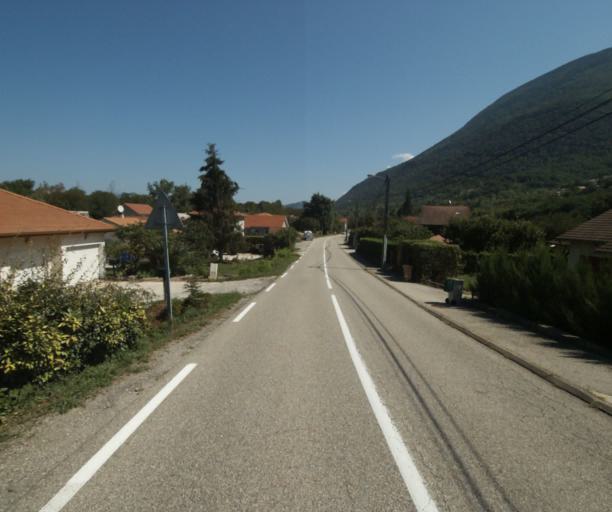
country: FR
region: Rhone-Alpes
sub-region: Departement de l'Isere
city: Saint-Georges-de-Commiers
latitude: 45.0446
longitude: 5.7006
